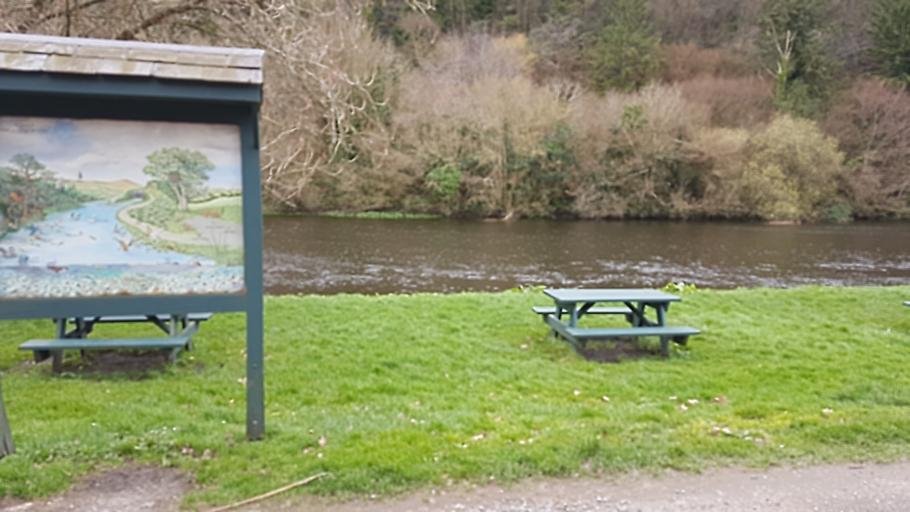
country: IE
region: Leinster
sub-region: Kilkenny
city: Graiguenamanagh
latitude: 52.4876
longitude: -6.9287
